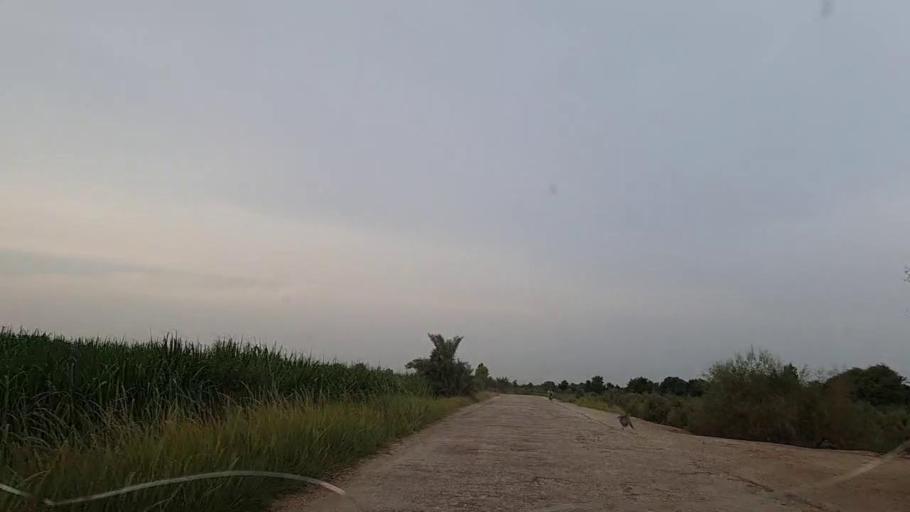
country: PK
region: Sindh
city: Mirpur Mathelo
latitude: 27.8839
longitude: 69.6388
